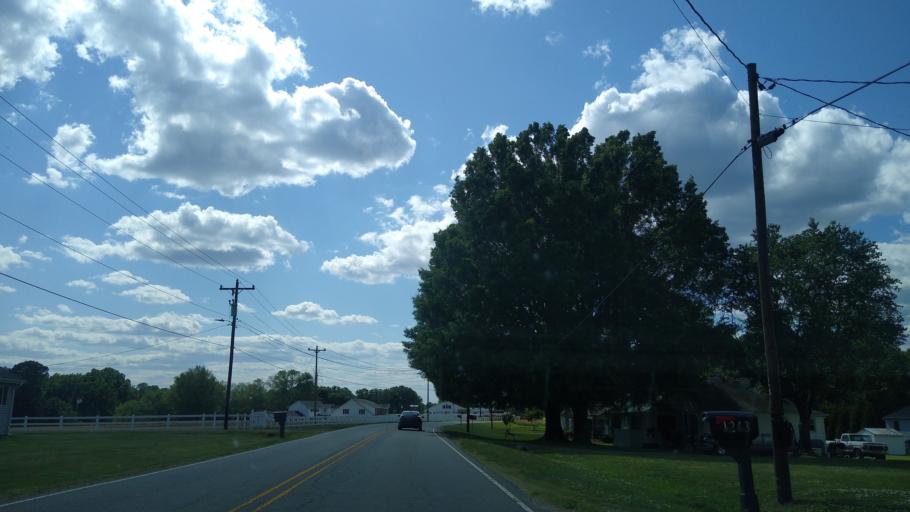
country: US
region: North Carolina
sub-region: Forsyth County
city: Kernersville
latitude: 36.1006
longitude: -80.0852
